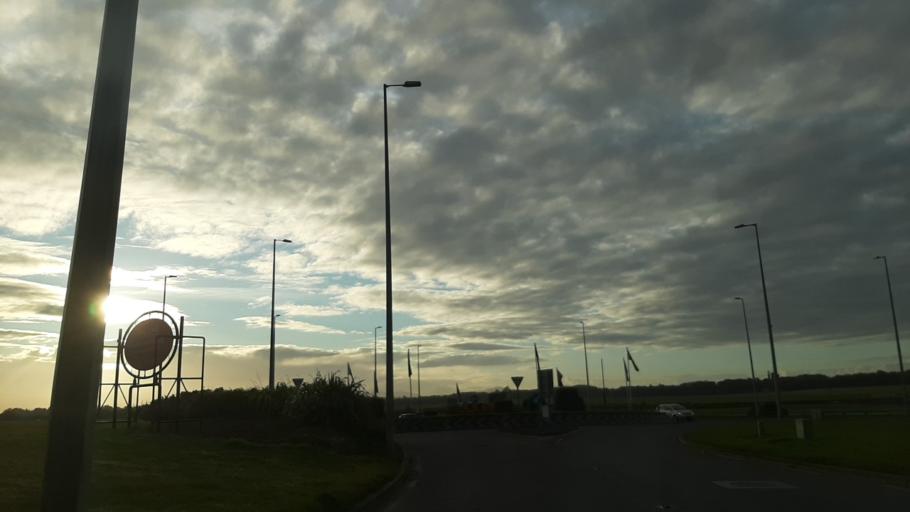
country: IE
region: Leinster
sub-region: Kildare
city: Athgarvan
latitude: 53.1666
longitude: -6.8380
